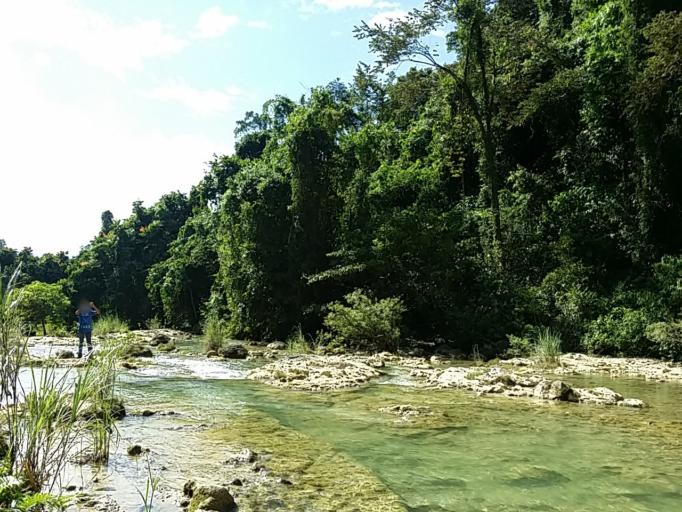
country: PH
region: Caraga
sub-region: Province of Agusan del Sur
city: Los Arcos
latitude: 8.6997
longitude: 125.9757
